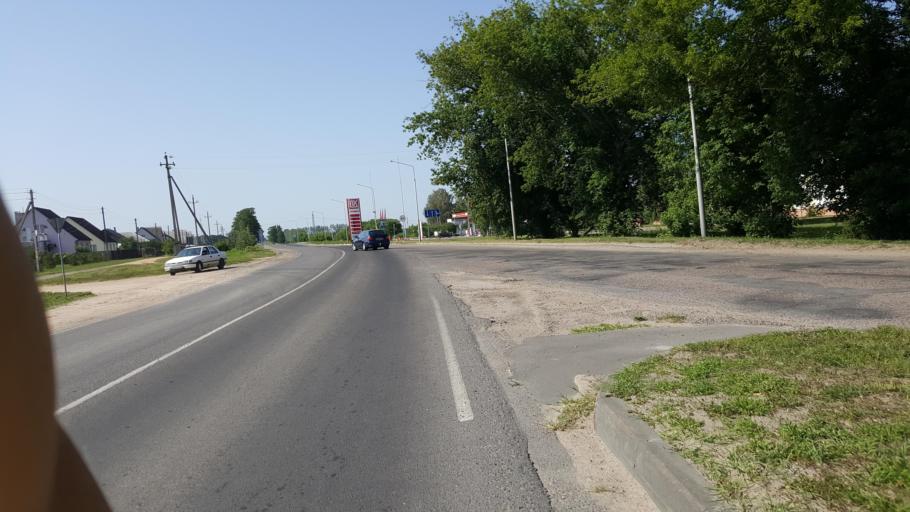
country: BY
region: Brest
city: Zhabinka
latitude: 52.2046
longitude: 24.0053
